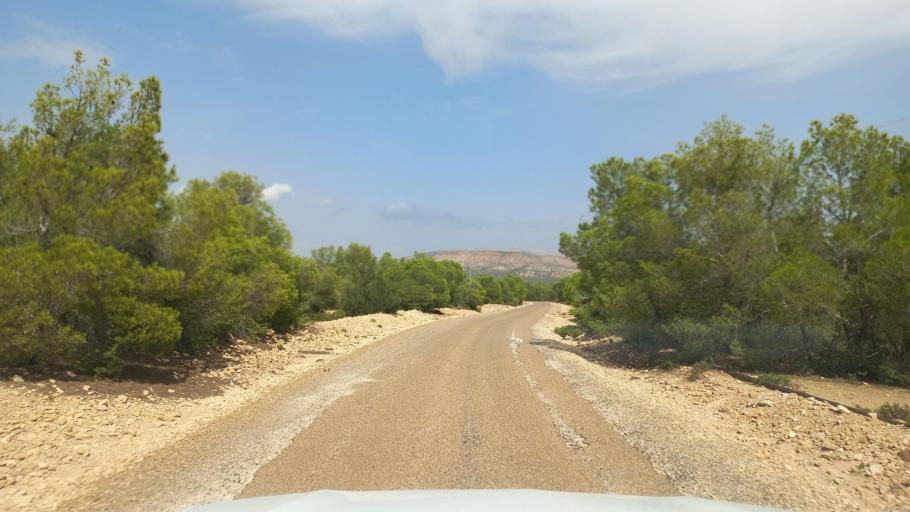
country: TN
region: Al Qasrayn
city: Sbiba
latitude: 35.3959
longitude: 8.9126
